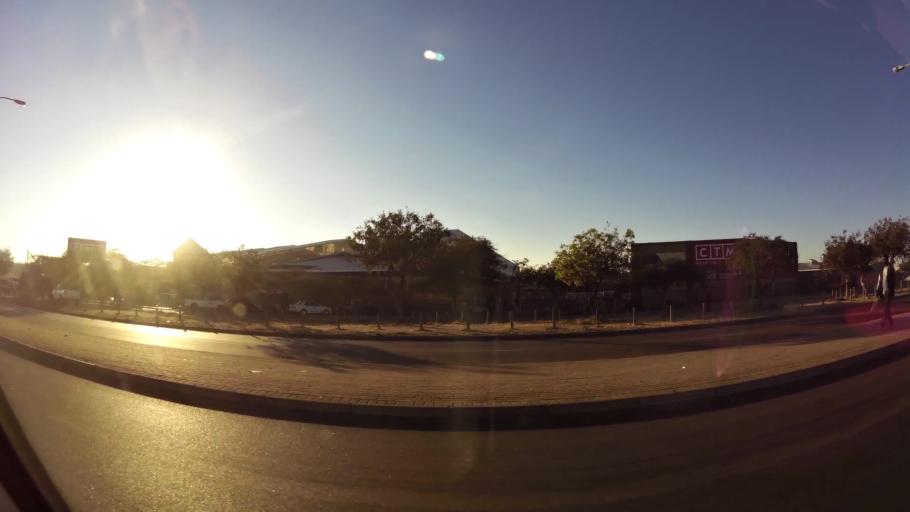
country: ZA
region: Limpopo
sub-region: Capricorn District Municipality
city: Polokwane
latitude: -23.9110
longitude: 29.4399
